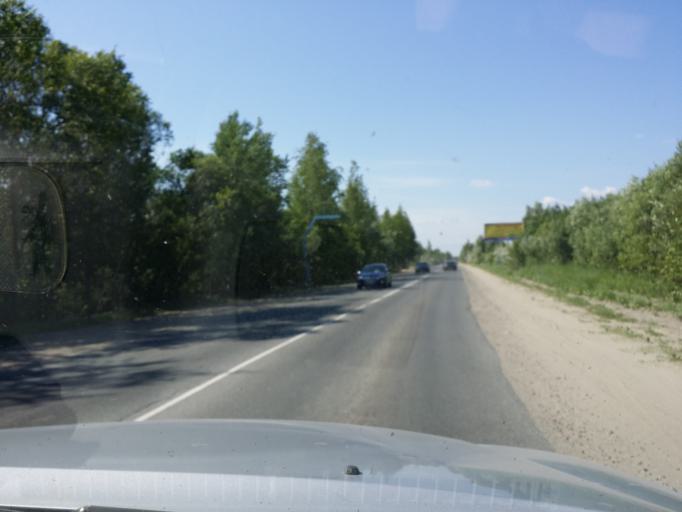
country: RU
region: Tomsk
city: Strezhevoy
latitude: 60.7267
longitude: 77.5672
